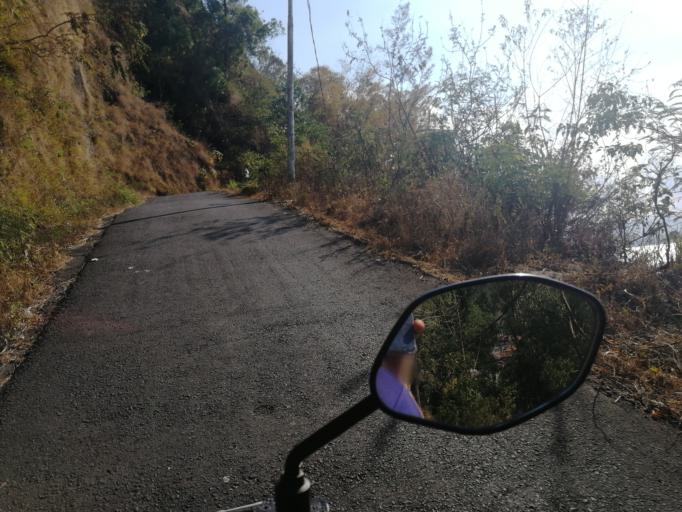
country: ID
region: Bali
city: Banjar Trunyan
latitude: -8.2550
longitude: 115.4253
